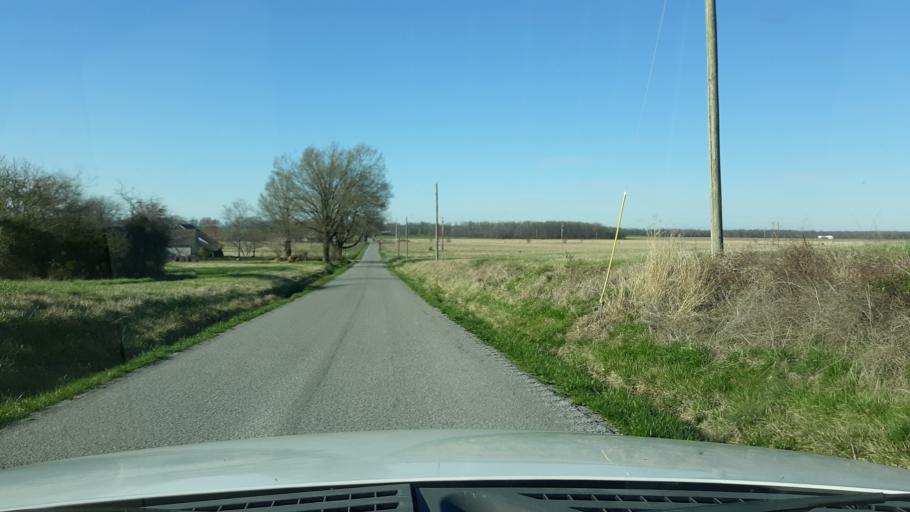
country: US
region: Illinois
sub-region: Saline County
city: Harrisburg
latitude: 37.7650
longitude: -88.5864
